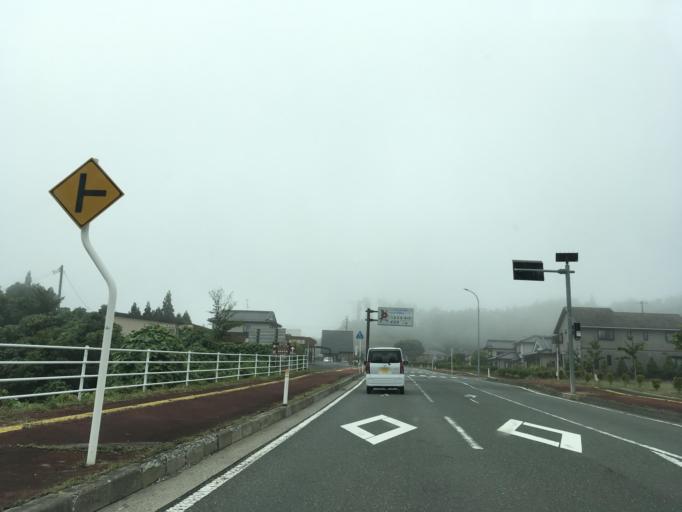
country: JP
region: Iwate
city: Ofunato
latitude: 38.9217
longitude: 141.6398
